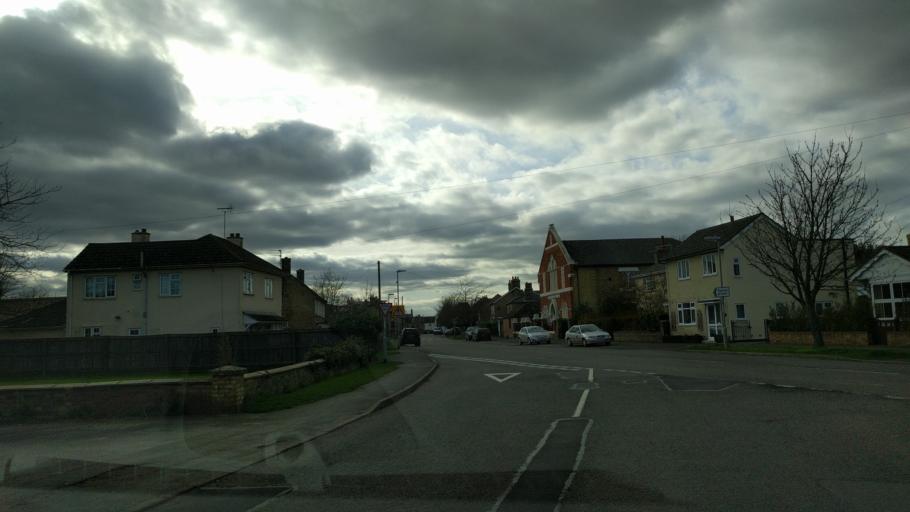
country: GB
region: England
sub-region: Cambridgeshire
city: Warboys
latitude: 52.4038
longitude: -0.0764
